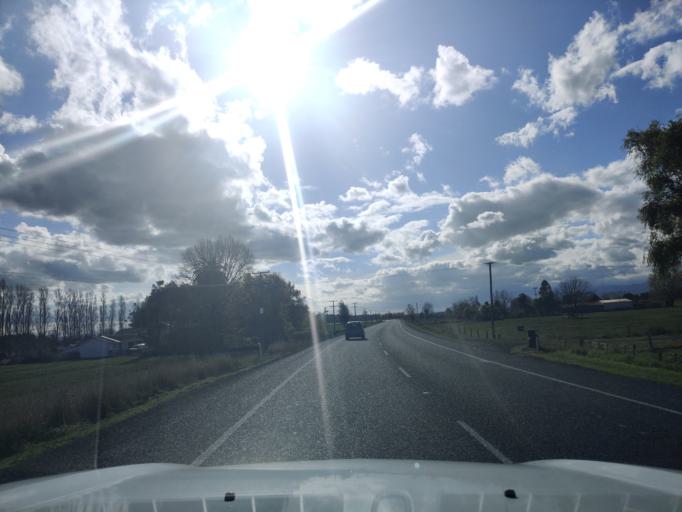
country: NZ
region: Waikato
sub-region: Hauraki District
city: Ngatea
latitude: -37.2779
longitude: 175.5328
